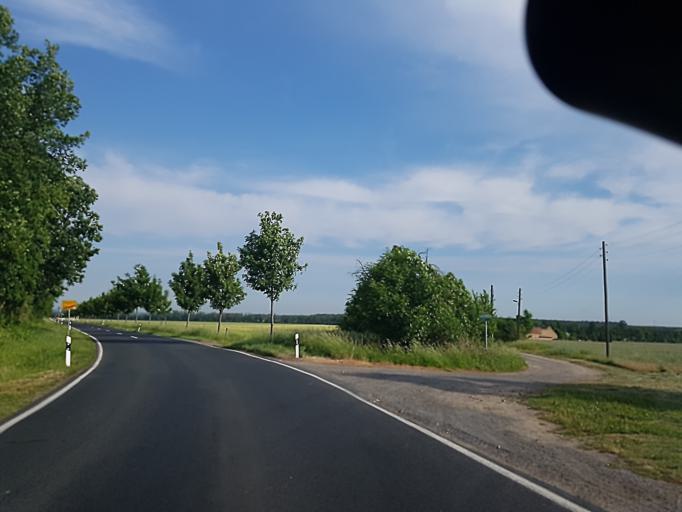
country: DE
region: Saxony-Anhalt
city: Kropstadt
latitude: 52.0288
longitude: 12.7382
